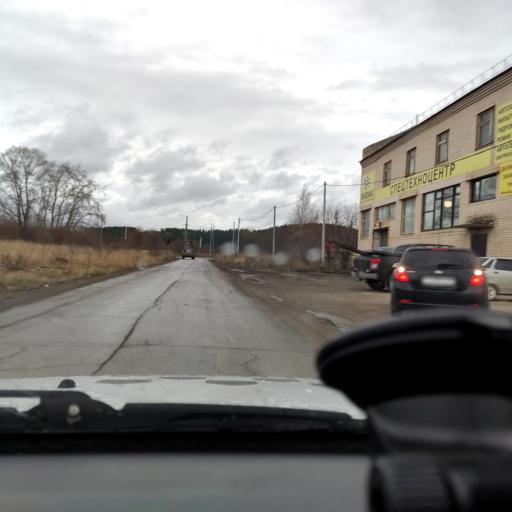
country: RU
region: Perm
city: Kondratovo
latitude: 57.9452
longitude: 56.1458
